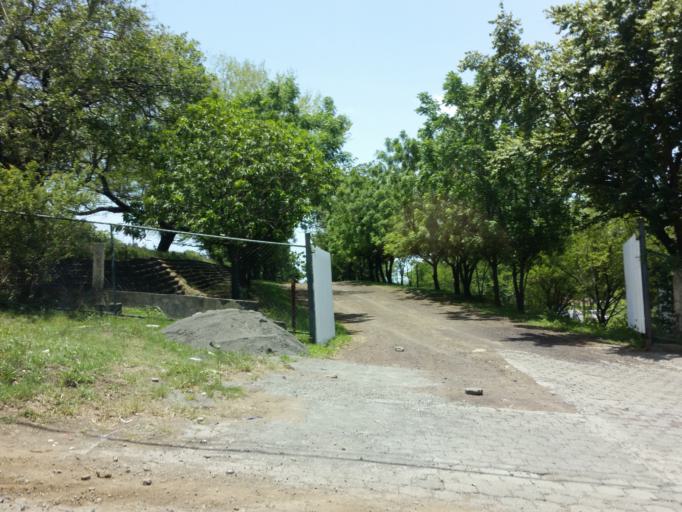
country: NI
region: Managua
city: Managua
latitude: 12.1149
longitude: -86.2732
